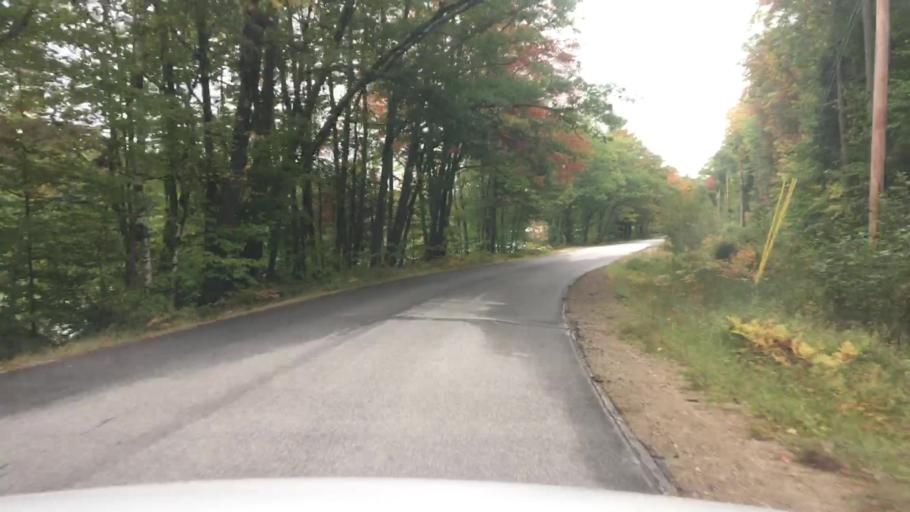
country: US
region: Maine
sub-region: Oxford County
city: Bethel
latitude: 44.4846
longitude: -70.7689
